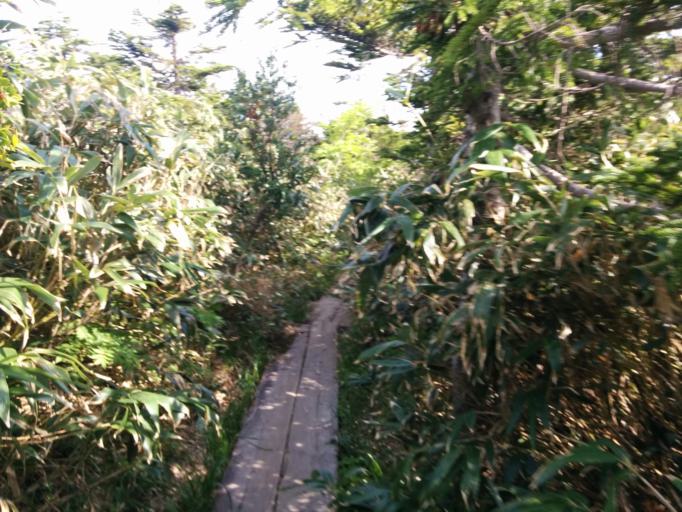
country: JP
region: Aomori
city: Aomori Shi
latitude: 40.6742
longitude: 140.8666
